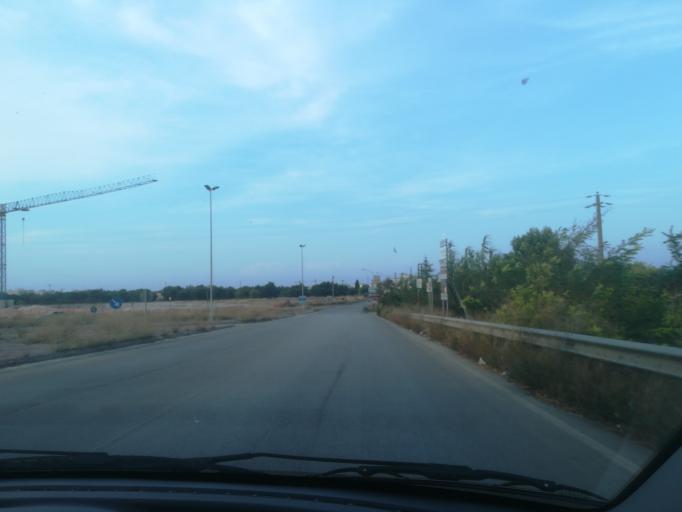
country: IT
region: Apulia
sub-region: Provincia di Bari
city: Monopoli
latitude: 40.9367
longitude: 17.2930
